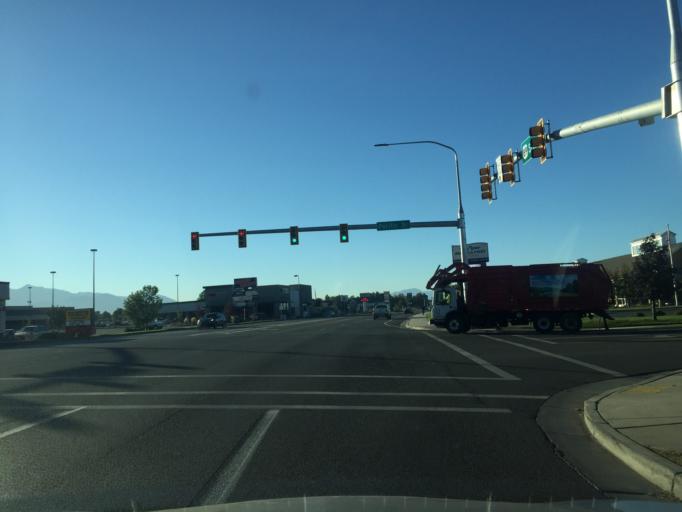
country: US
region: Utah
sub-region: Utah County
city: American Fork
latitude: 40.3832
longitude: -111.8148
